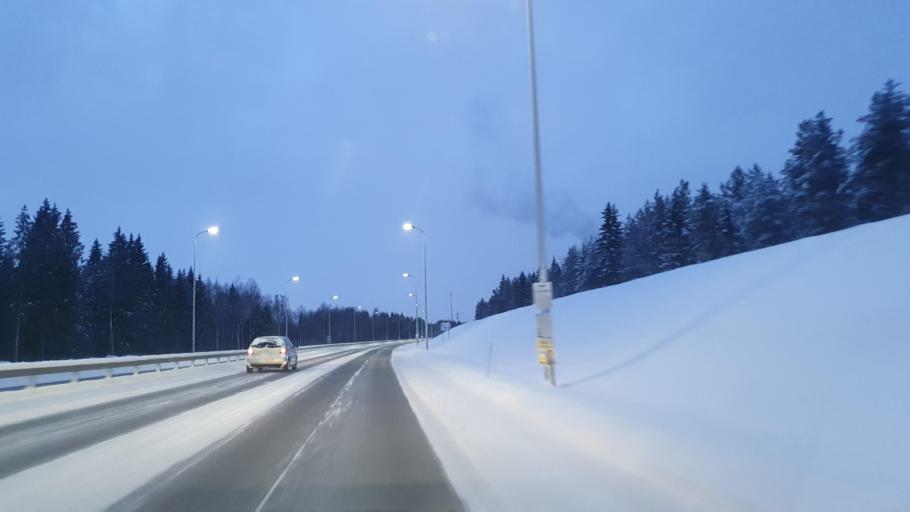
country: FI
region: Northern Ostrobothnia
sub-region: Oulu
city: Kempele
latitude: 64.9832
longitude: 25.5531
